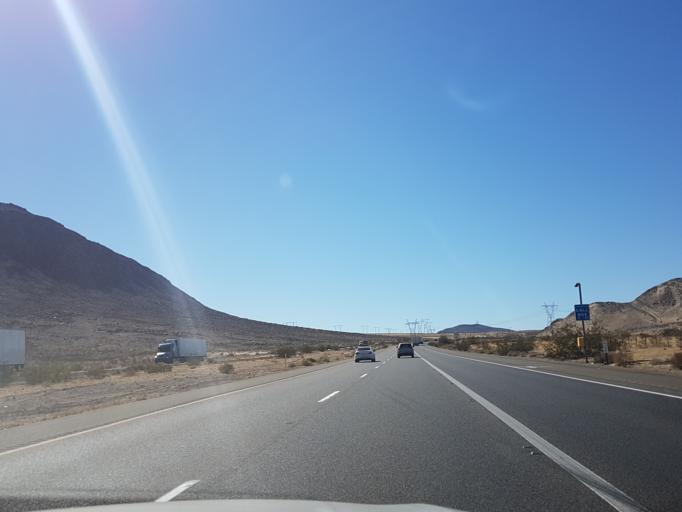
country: US
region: California
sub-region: San Bernardino County
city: Fort Irwin
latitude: 35.0905
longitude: -116.3134
